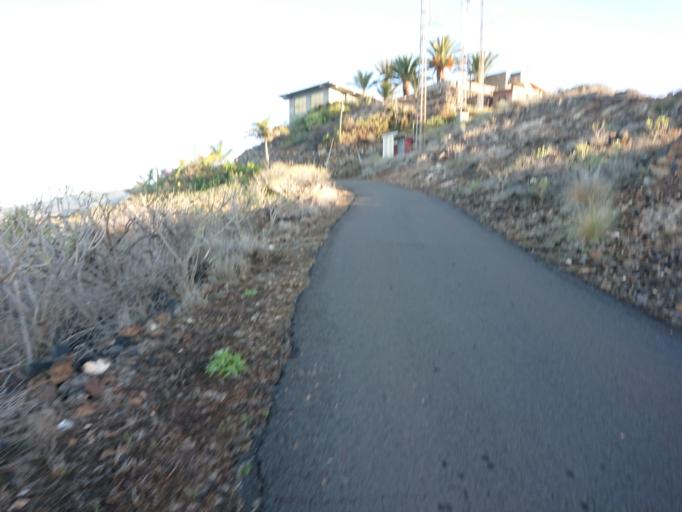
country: ES
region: Canary Islands
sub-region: Provincia de Santa Cruz de Tenerife
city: Tazacorte
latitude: 28.6628
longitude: -17.9431
